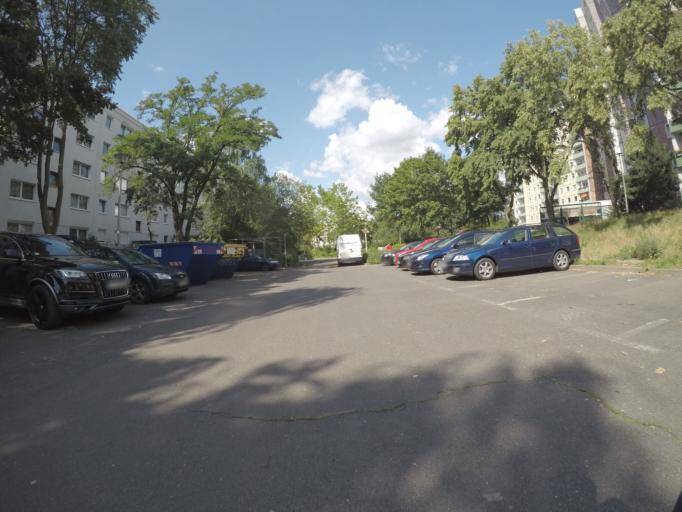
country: DE
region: Berlin
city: Kaulsdorf
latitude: 52.5195
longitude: 13.5827
